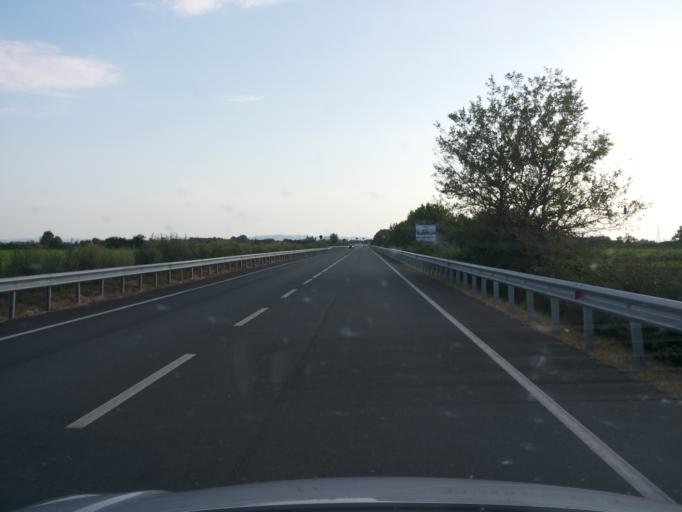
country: IT
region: Piedmont
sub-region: Provincia di Vercelli
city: Desana
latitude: 45.2852
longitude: 8.3752
